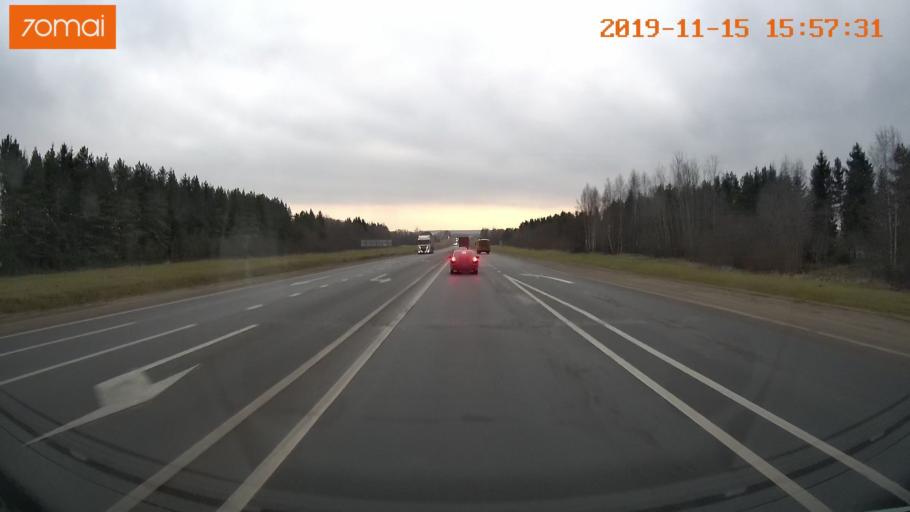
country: RU
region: Jaroslavl
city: Yaroslavl
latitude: 57.8294
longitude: 39.9627
